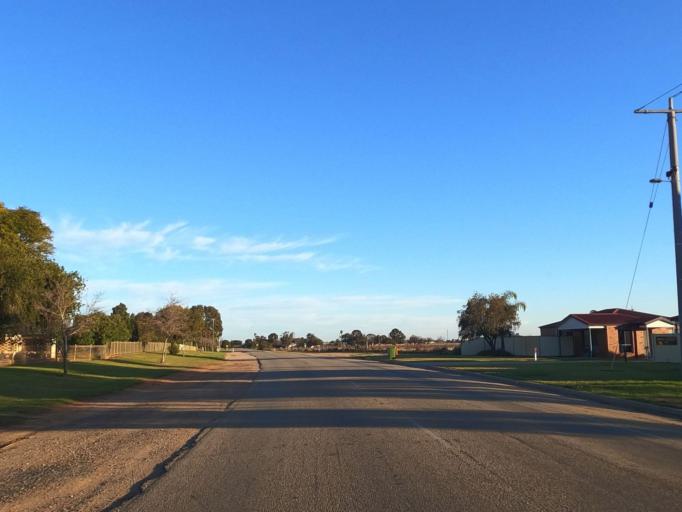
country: AU
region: Victoria
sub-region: Swan Hill
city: Swan Hill
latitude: -35.3540
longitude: 143.5529
